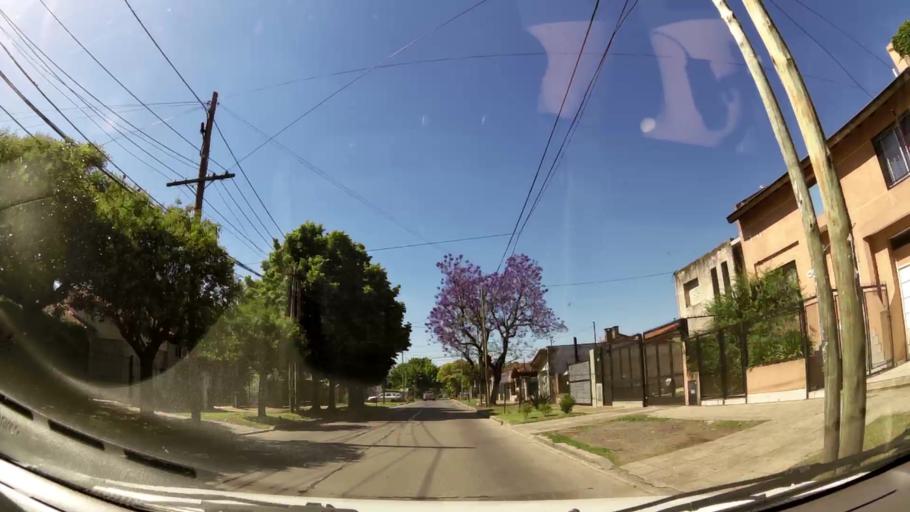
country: AR
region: Buenos Aires
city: Ituzaingo
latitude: -34.6497
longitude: -58.6638
